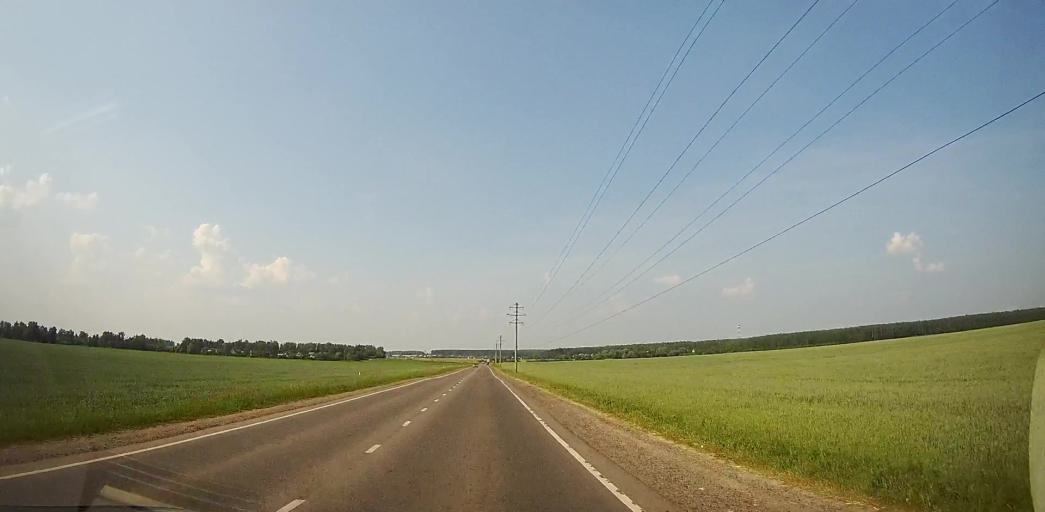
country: RU
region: Moskovskaya
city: Barybino
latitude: 55.2554
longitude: 37.9188
